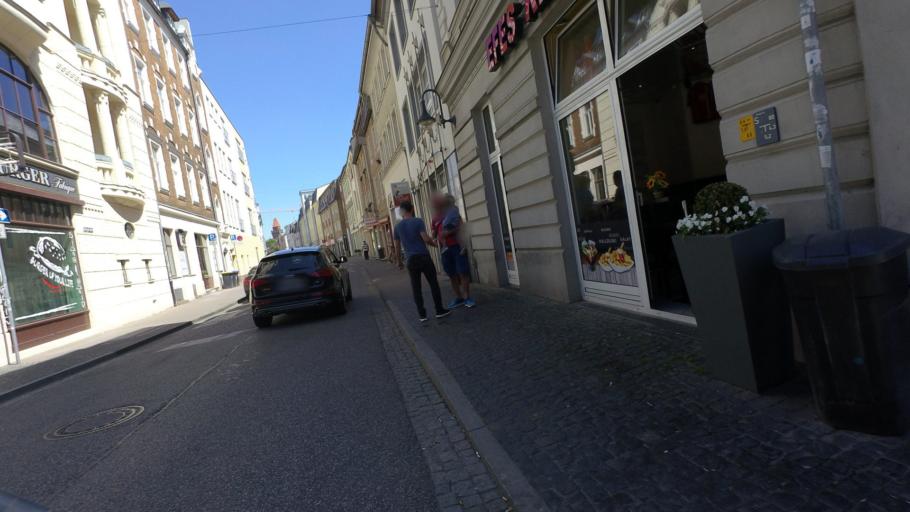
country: DE
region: Brandenburg
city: Cottbus
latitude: 51.7579
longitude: 14.3336
